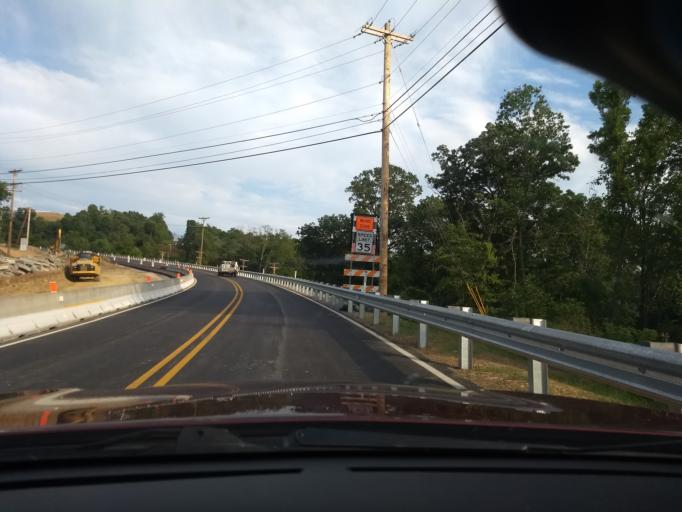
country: US
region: Pennsylvania
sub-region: Armstrong County
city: Freeport
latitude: 40.6640
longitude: -79.6888
